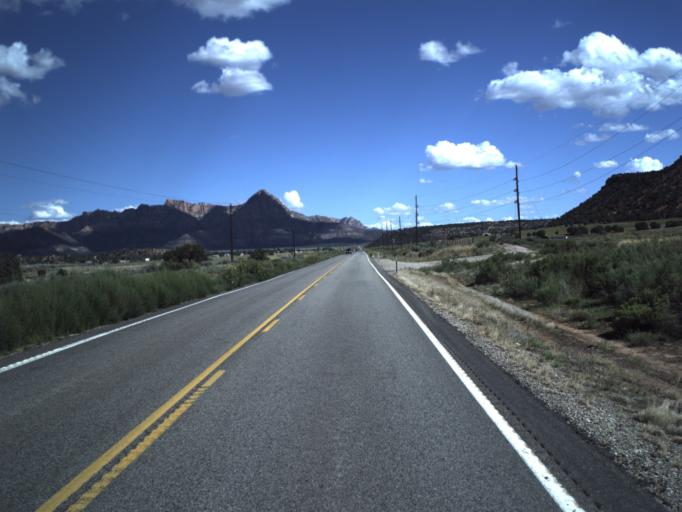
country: US
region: Utah
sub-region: Washington County
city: LaVerkin
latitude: 37.1160
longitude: -113.1560
